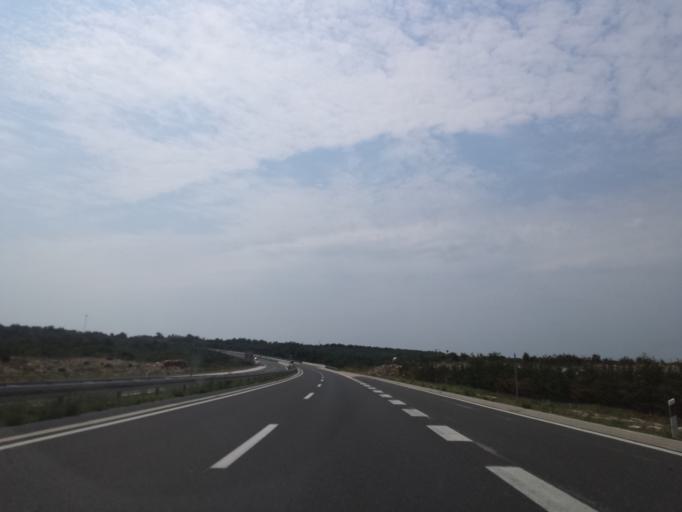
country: HR
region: Zadarska
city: Posedarje
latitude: 44.2158
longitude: 15.4517
